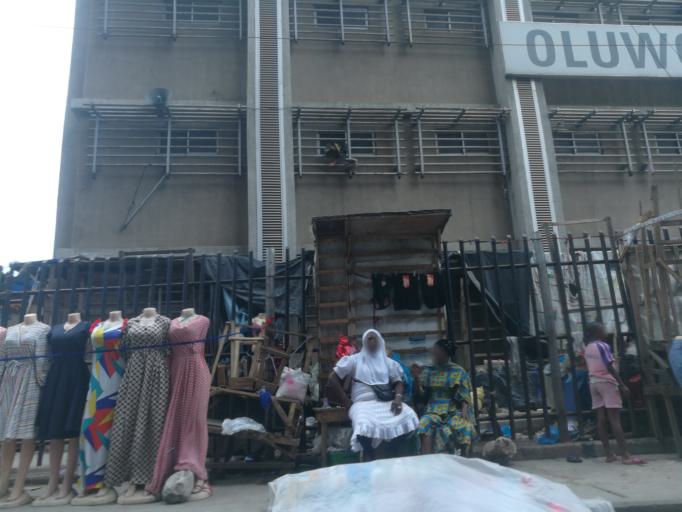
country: NG
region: Lagos
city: Lagos
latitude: 6.4578
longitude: 3.3862
